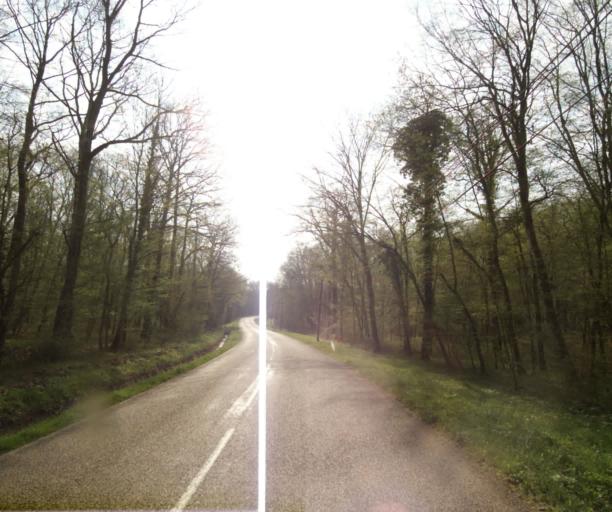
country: FR
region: Bourgogne
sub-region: Departement de Saone-et-Loire
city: Charolles
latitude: 46.4538
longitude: 4.2595
